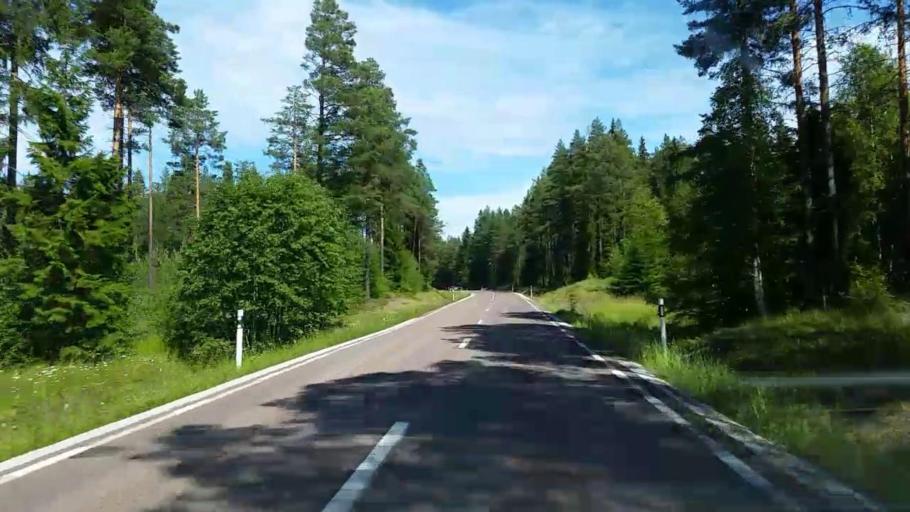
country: SE
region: Dalarna
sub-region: Rattviks Kommun
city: Raettvik
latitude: 60.9095
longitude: 15.1981
